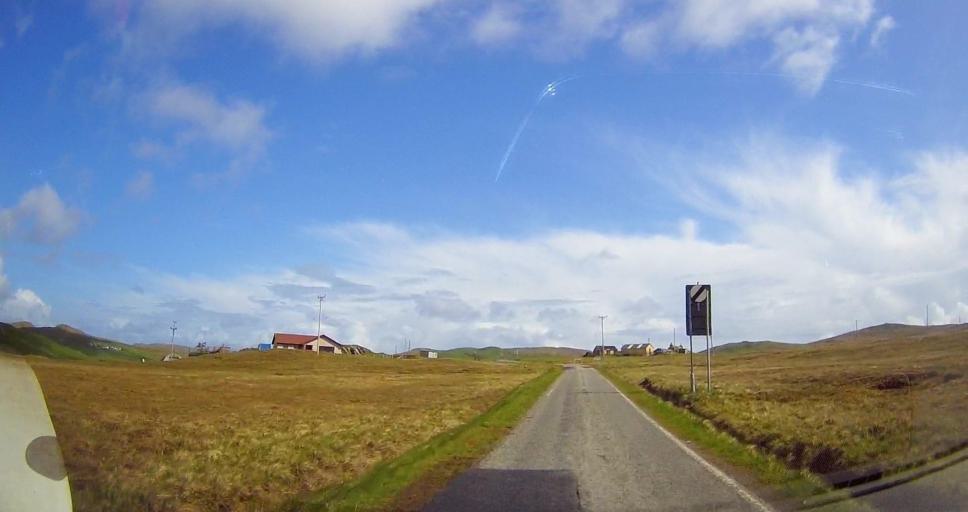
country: GB
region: Scotland
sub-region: Shetland Islands
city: Lerwick
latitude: 60.5877
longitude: -1.3354
